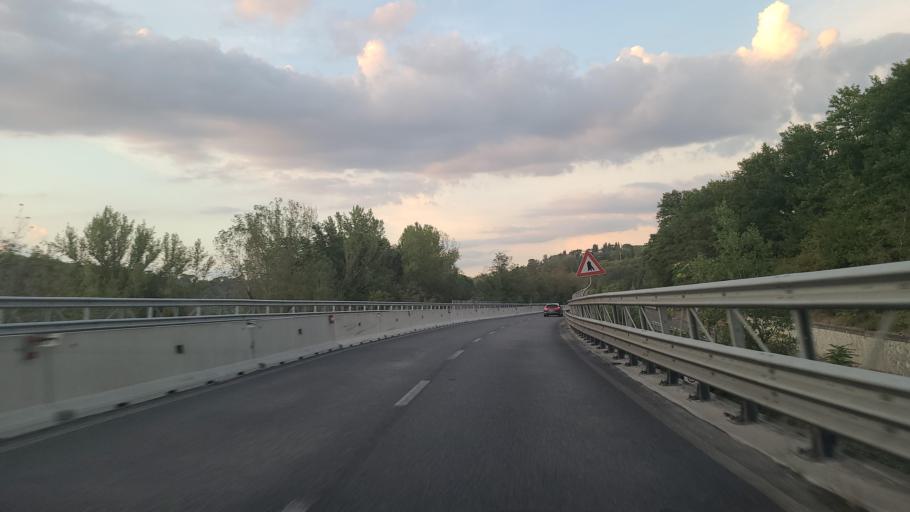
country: IT
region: Tuscany
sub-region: Province of Florence
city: Tavarnuzze
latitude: 43.6885
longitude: 11.2111
